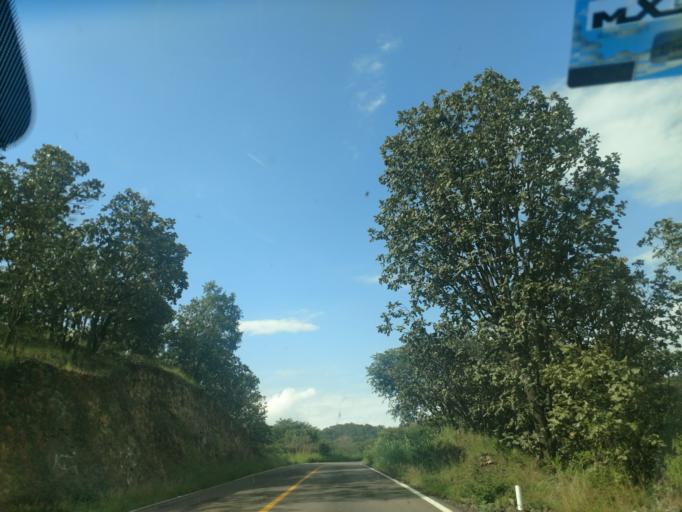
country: MX
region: Jalisco
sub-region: Atengo
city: Soyatlan del Oro
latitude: 20.4980
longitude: -104.3561
